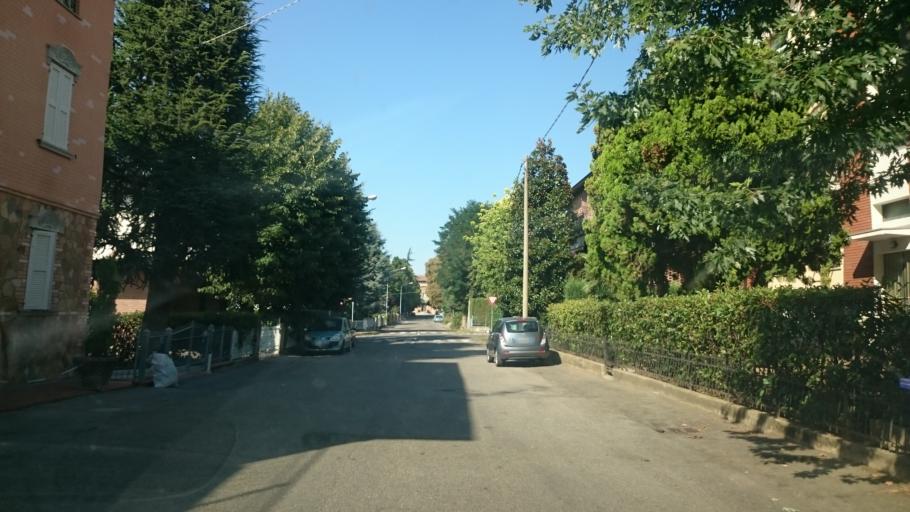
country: IT
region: Emilia-Romagna
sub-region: Provincia di Reggio Emilia
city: Ventoso
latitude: 44.5954
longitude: 10.6846
